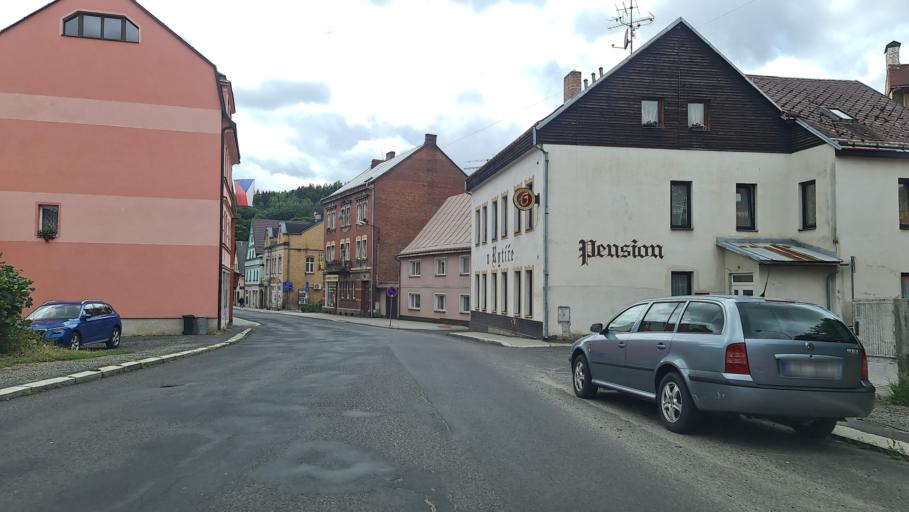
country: CZ
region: Karlovarsky
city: Kraslice
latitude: 50.3299
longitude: 12.5125
